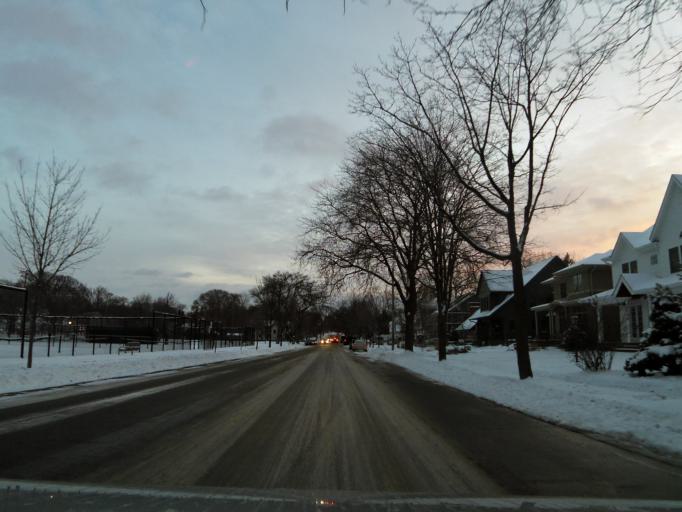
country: US
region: Minnesota
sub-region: Hennepin County
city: Saint Louis Park
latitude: 44.9268
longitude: -93.3215
